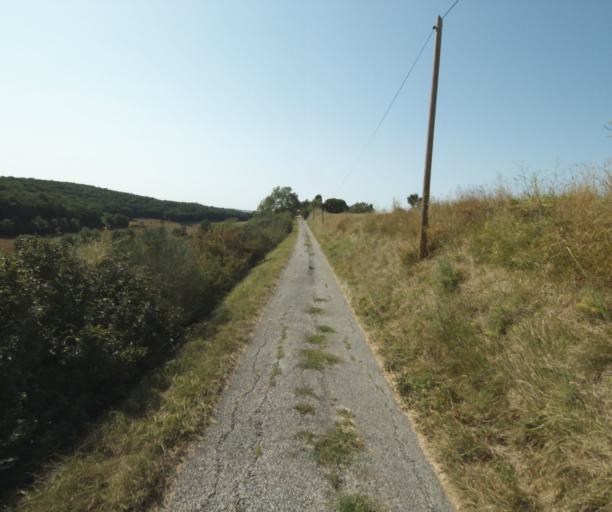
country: FR
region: Midi-Pyrenees
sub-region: Departement de la Haute-Garonne
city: Saint-Felix-Lauragais
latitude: 43.4306
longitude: 1.8453
